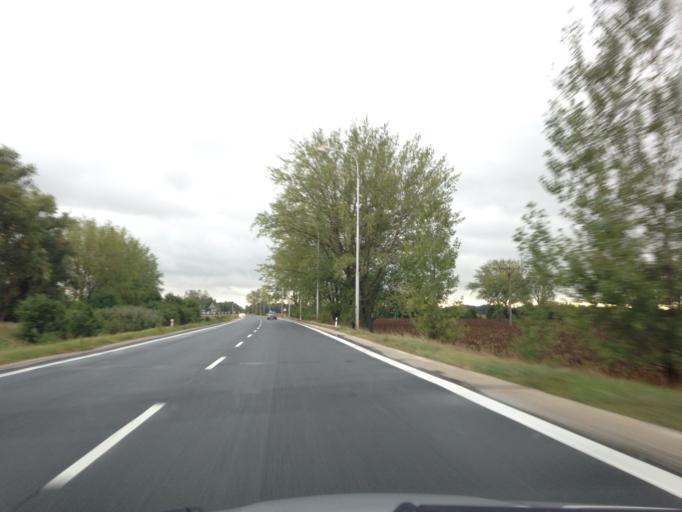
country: SK
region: Nitriansky
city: Komarno
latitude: 47.7866
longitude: 18.1672
